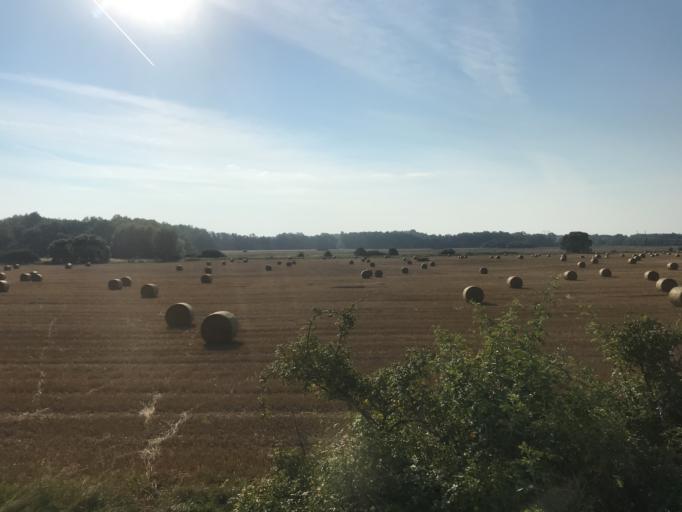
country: CZ
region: Jihocesky
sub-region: Okres Jindrichuv Hradec
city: Lomnice nad Luznici
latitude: 49.1011
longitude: 14.7353
